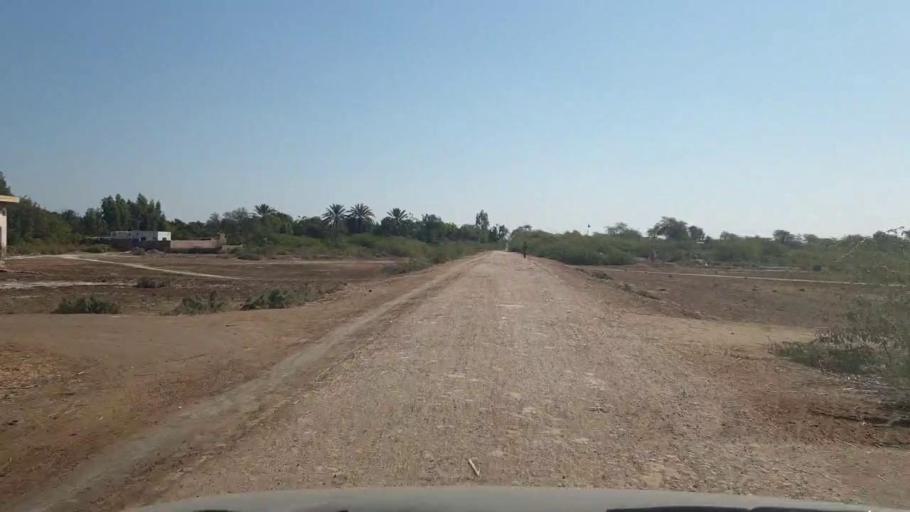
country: PK
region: Sindh
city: Mirwah Gorchani
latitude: 25.2916
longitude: 69.1241
